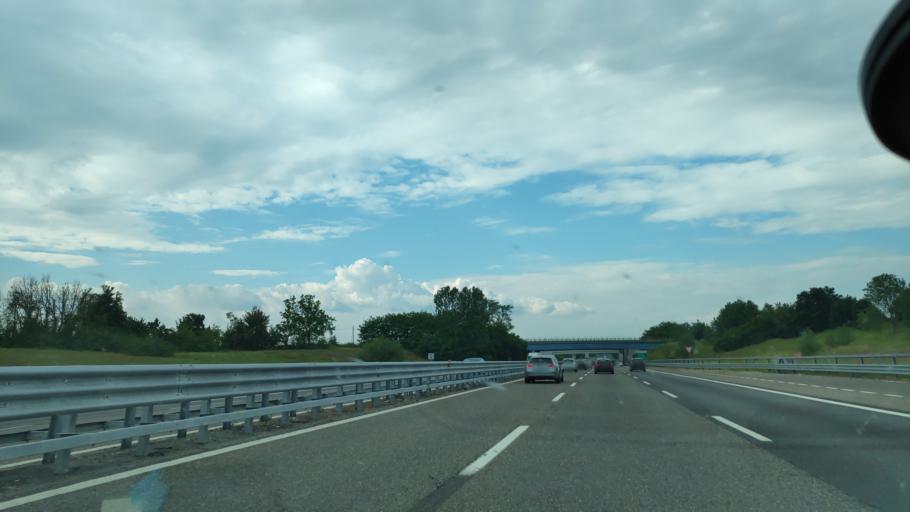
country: IT
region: Lombardy
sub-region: Provincia di Pavia
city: Pieve Albignola
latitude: 45.1158
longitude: 8.9763
